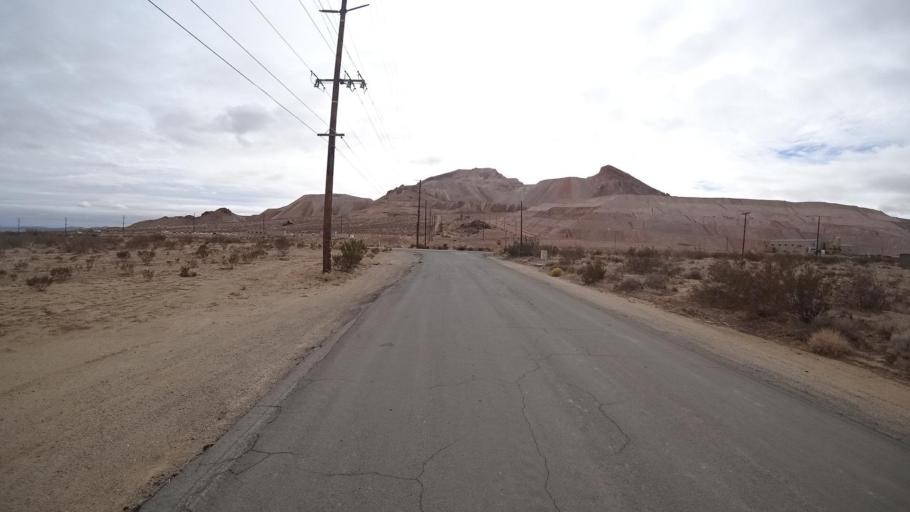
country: US
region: California
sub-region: Kern County
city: Mojave
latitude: 34.9975
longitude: -118.1858
